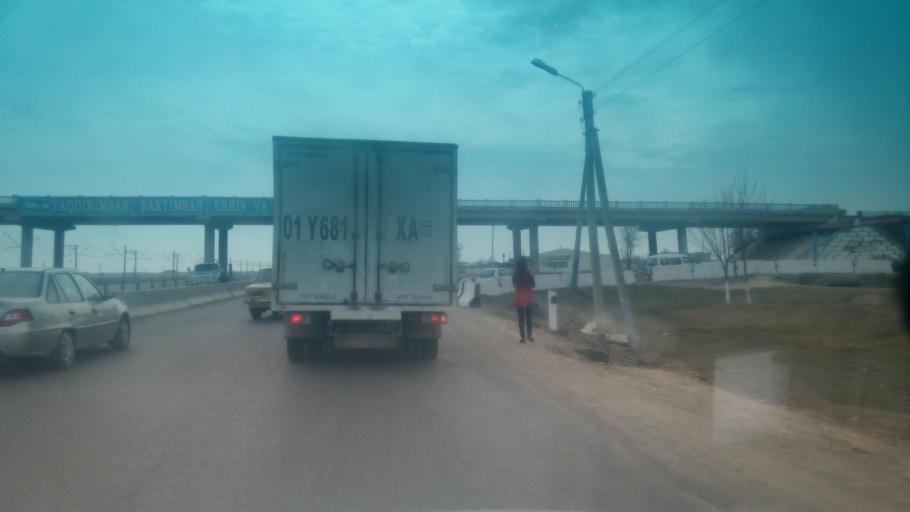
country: UZ
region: Sirdaryo
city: Guliston
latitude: 40.4723
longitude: 68.7716
